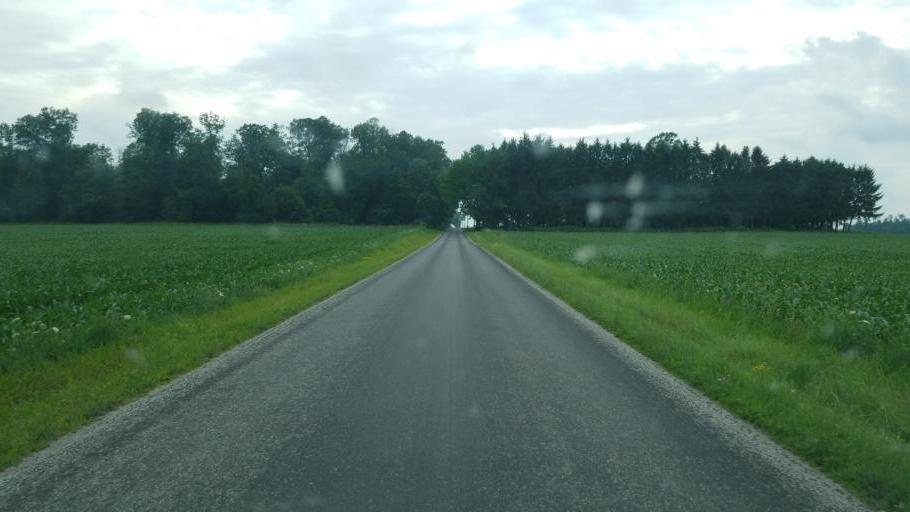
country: US
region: Ohio
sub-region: Wayne County
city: Apple Creek
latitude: 40.7777
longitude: -81.8286
